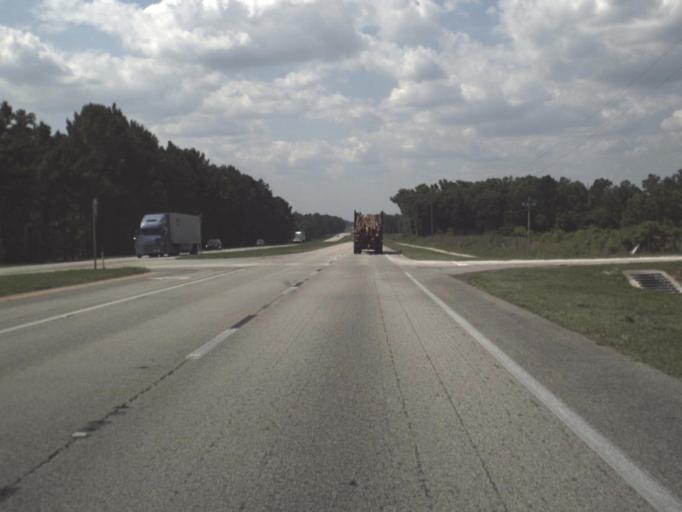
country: US
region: Florida
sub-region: Alachua County
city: Hawthorne
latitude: 29.6696
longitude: -82.1190
